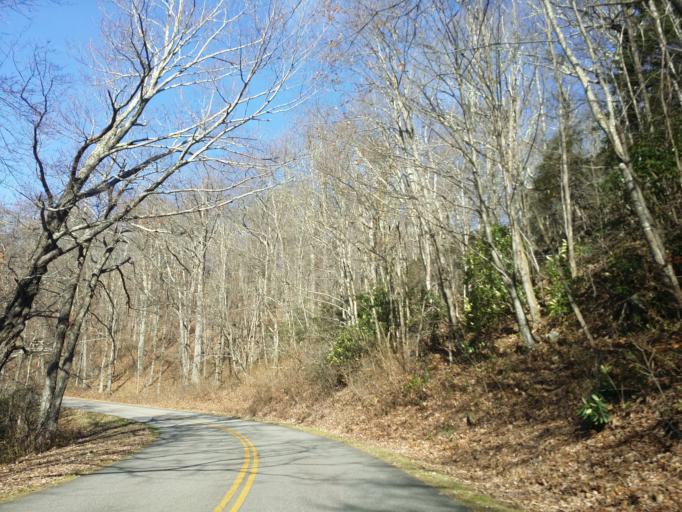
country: US
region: North Carolina
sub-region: Mitchell County
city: Spruce Pine
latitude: 35.7803
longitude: -82.1596
